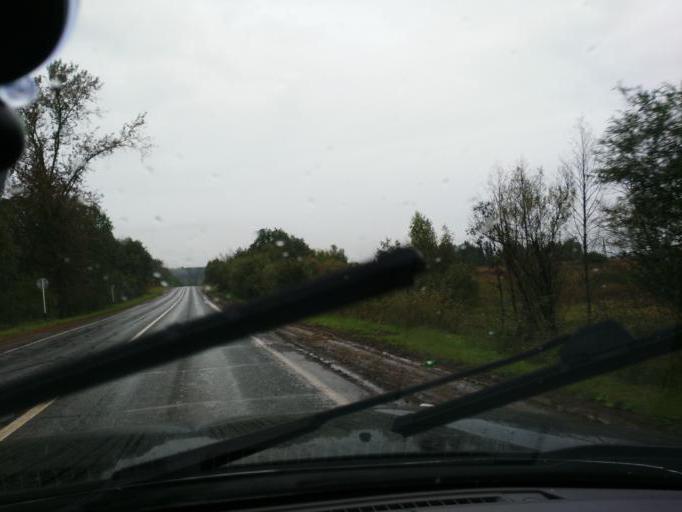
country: RU
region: Perm
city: Yugo-Kamskiy
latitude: 57.5357
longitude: 55.6891
